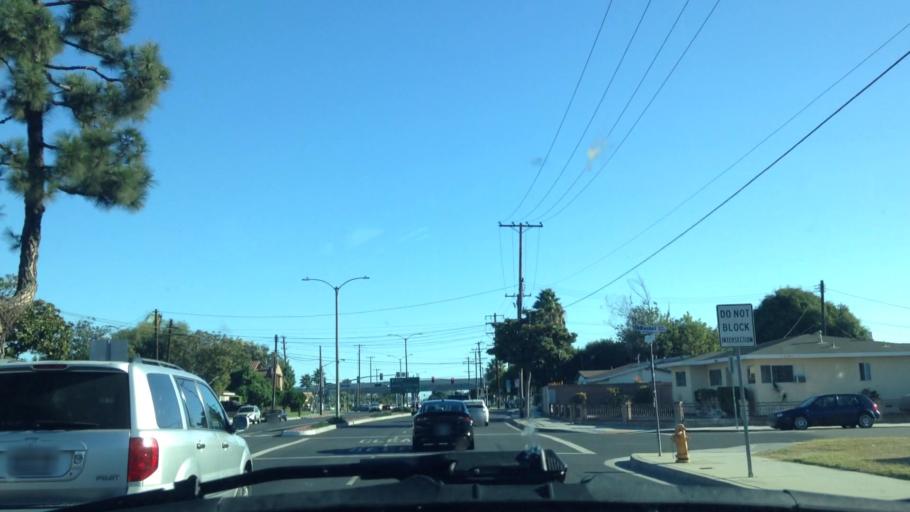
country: US
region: California
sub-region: Orange County
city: Midway City
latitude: 33.7686
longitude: -117.9725
